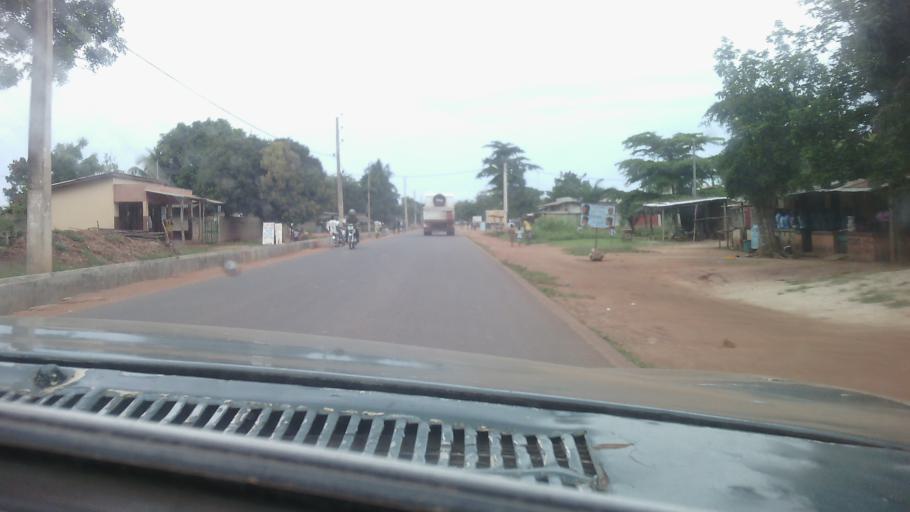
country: BJ
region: Mono
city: Come
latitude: 6.5193
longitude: 1.8215
